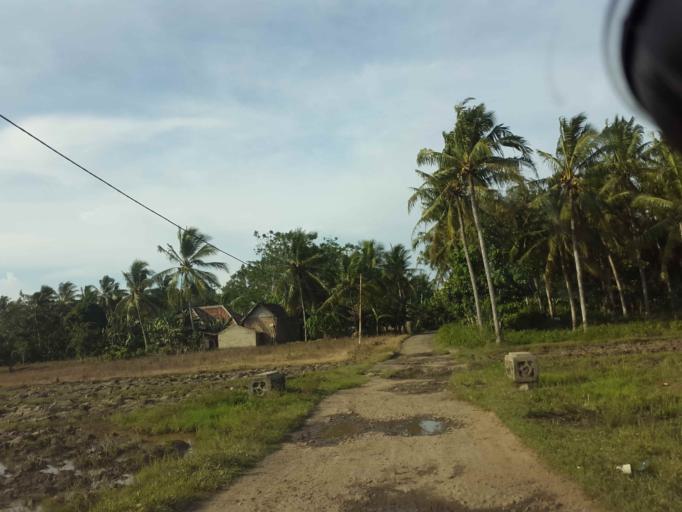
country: ID
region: Lampung
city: Palas
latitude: -5.6943
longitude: 105.6548
